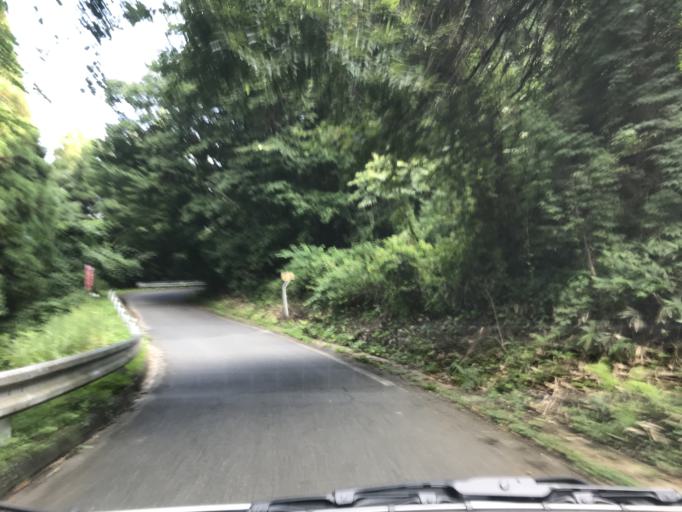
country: JP
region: Iwate
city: Ofunato
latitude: 38.9815
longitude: 141.4683
